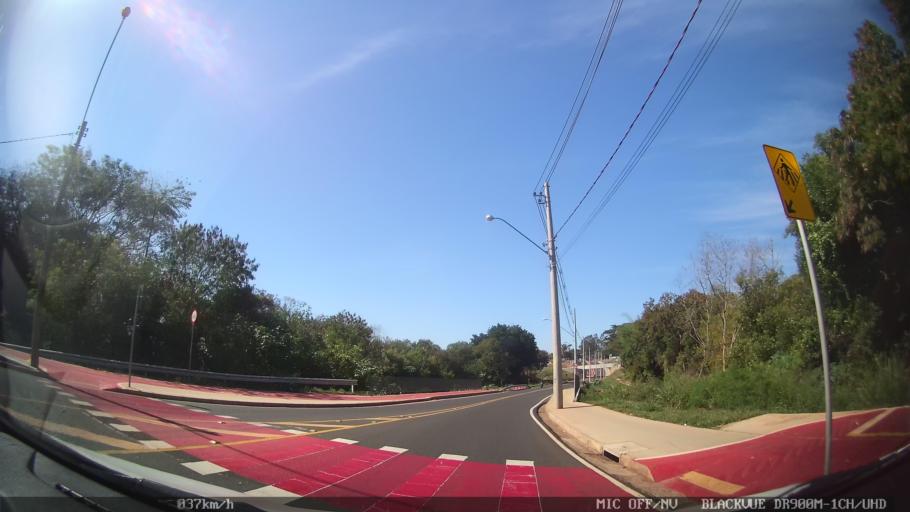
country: BR
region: Sao Paulo
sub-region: Sao Jose Do Rio Preto
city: Sao Jose do Rio Preto
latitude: -20.8063
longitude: -49.4244
